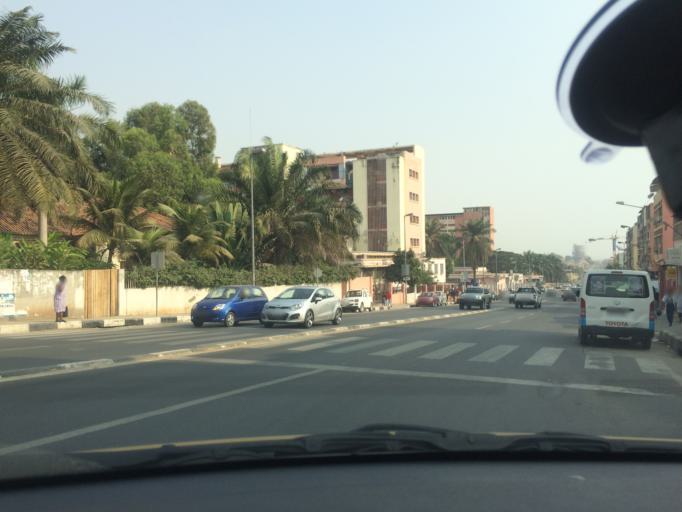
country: AO
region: Luanda
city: Luanda
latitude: -8.8251
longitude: 13.2248
